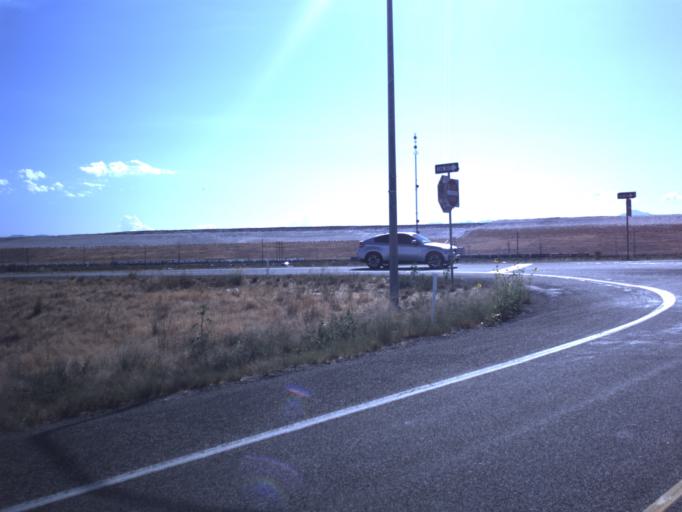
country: US
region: Utah
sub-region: Salt Lake County
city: Magna
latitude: 40.7464
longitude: -112.1848
